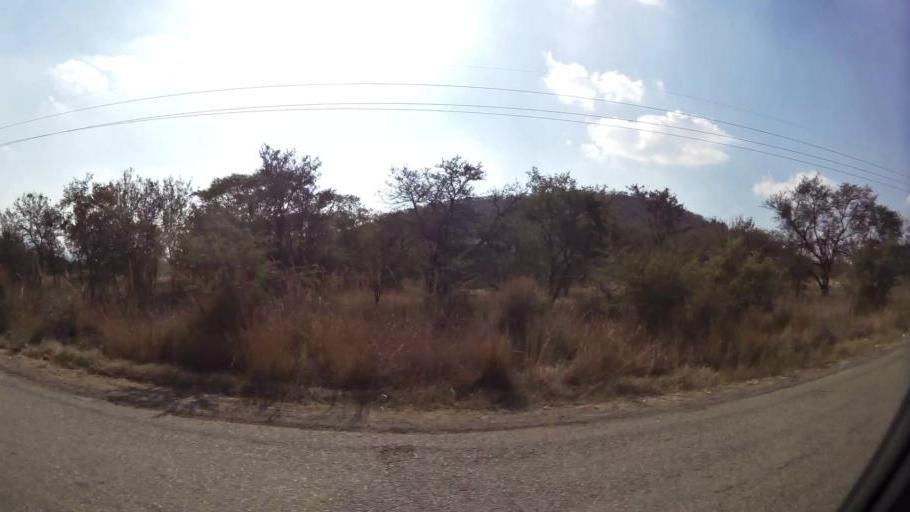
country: ZA
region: North-West
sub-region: Bojanala Platinum District Municipality
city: Rustenburg
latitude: -25.6322
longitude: 27.1774
